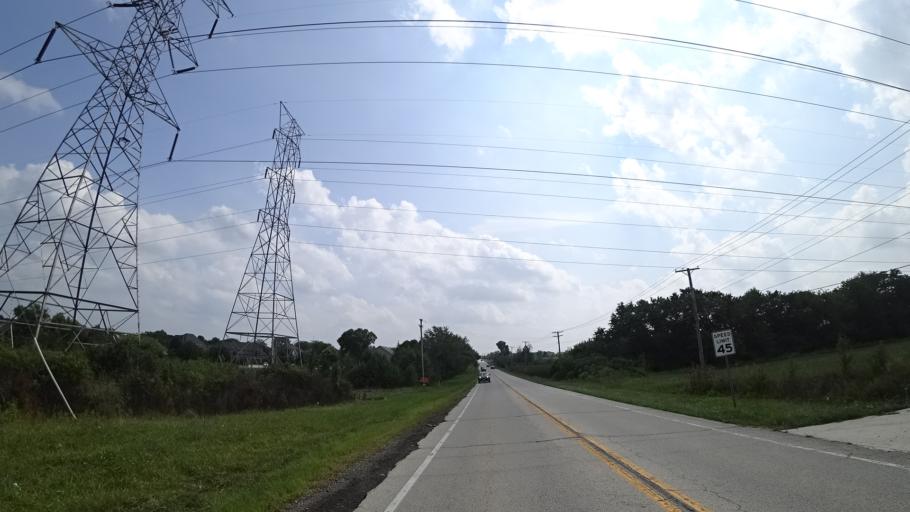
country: US
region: Illinois
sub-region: Will County
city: Goodings Grove
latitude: 41.6412
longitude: -87.8926
